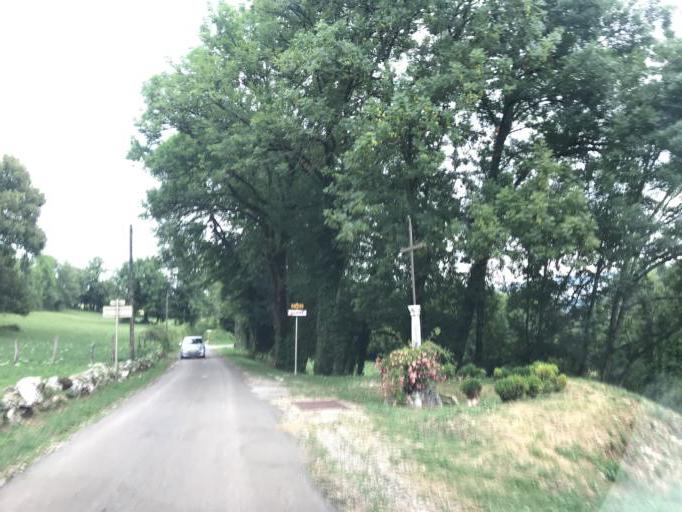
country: FR
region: Franche-Comte
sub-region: Departement du Jura
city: Lavans-les-Saint-Claude
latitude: 46.3281
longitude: 5.7502
